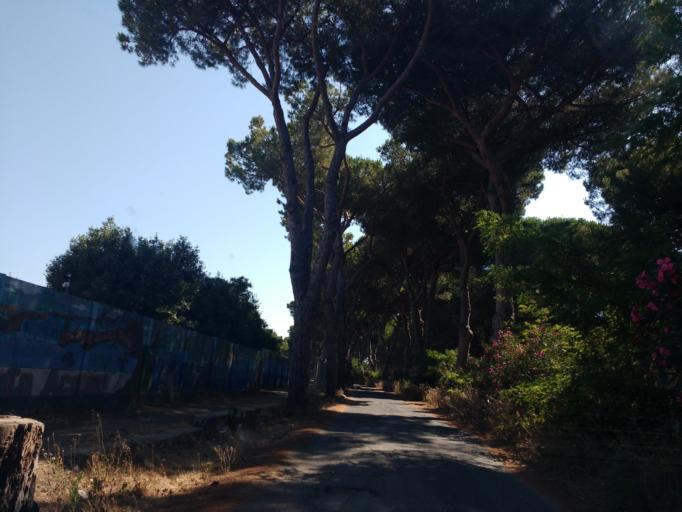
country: IT
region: Latium
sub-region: Citta metropolitana di Roma Capitale
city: Acilia-Castel Fusano-Ostia Antica
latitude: 41.7620
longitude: 12.3625
